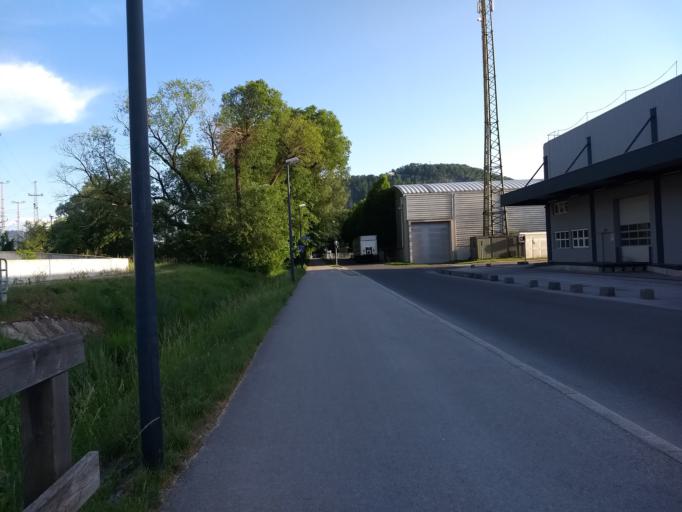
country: AT
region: Salzburg
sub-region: Salzburg Stadt
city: Salzburg
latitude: 47.8173
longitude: 13.0620
